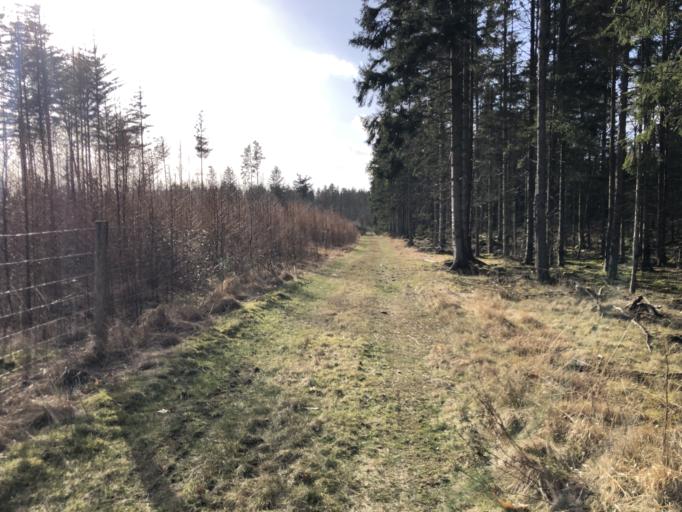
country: DK
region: Central Jutland
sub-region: Holstebro Kommune
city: Ulfborg
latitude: 56.2691
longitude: 8.4403
